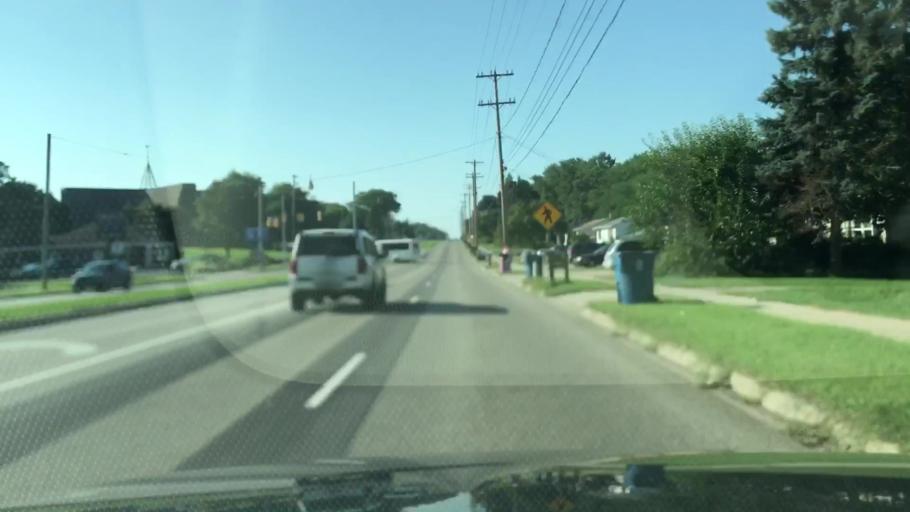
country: US
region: Michigan
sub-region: Kent County
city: Kentwood
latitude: 42.8684
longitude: -85.6254
